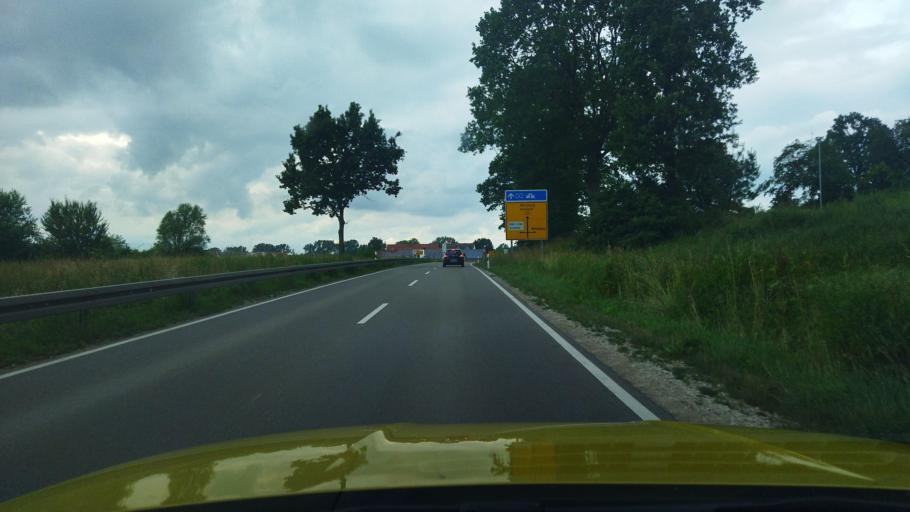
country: DE
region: Bavaria
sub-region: Regierungsbezirk Mittelfranken
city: Muhr am See
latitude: 49.1559
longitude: 10.7185
